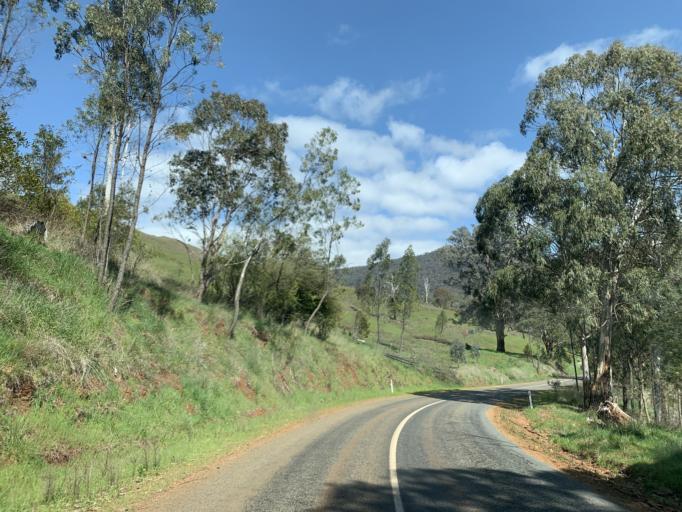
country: AU
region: Victoria
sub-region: Mansfield
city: Mansfield
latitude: -36.8274
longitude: 146.1289
